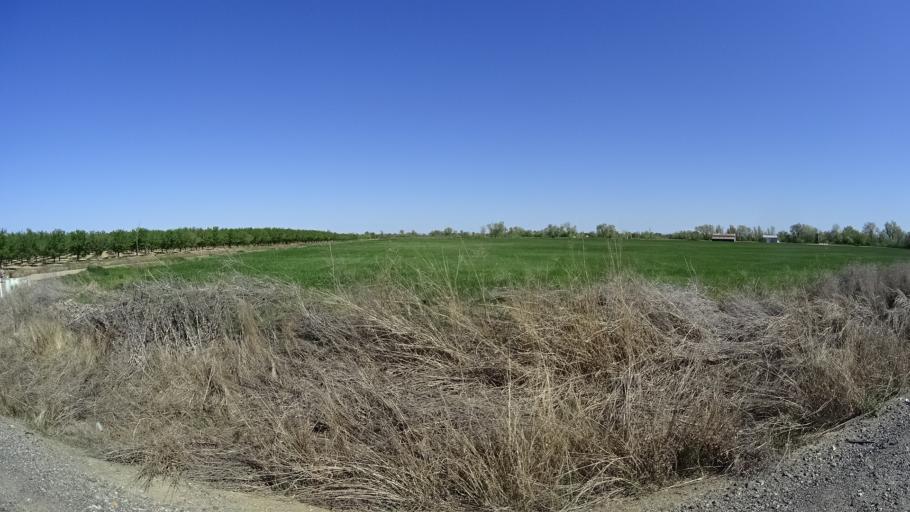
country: US
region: California
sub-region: Glenn County
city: Orland
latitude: 39.6972
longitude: -122.2326
